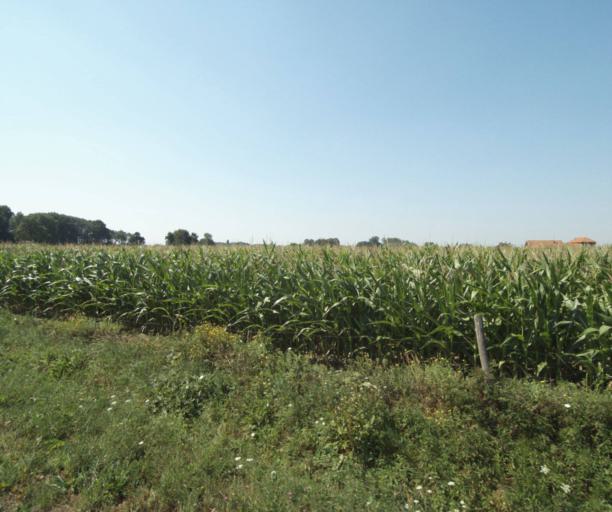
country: FR
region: Nord-Pas-de-Calais
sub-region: Departement du Nord
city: Wervicq-Sud
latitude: 50.7655
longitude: 3.0413
